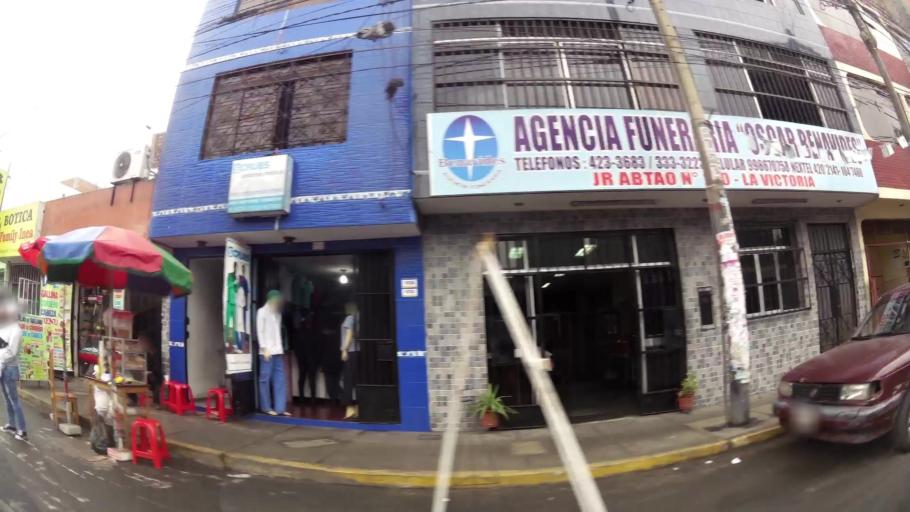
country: PE
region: Lima
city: Lima
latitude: -12.0595
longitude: -77.0231
